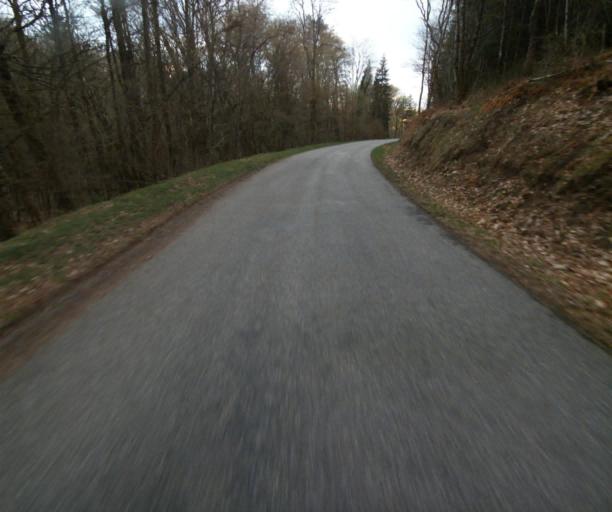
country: FR
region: Limousin
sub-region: Departement de la Correze
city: Argentat
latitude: 45.2521
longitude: 1.9826
